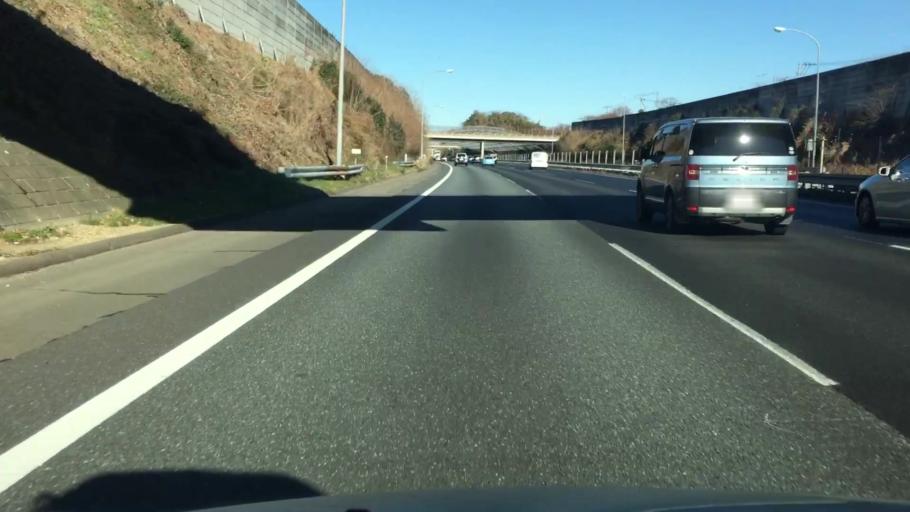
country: JP
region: Saitama
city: Sakado
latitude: 36.0062
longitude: 139.3873
